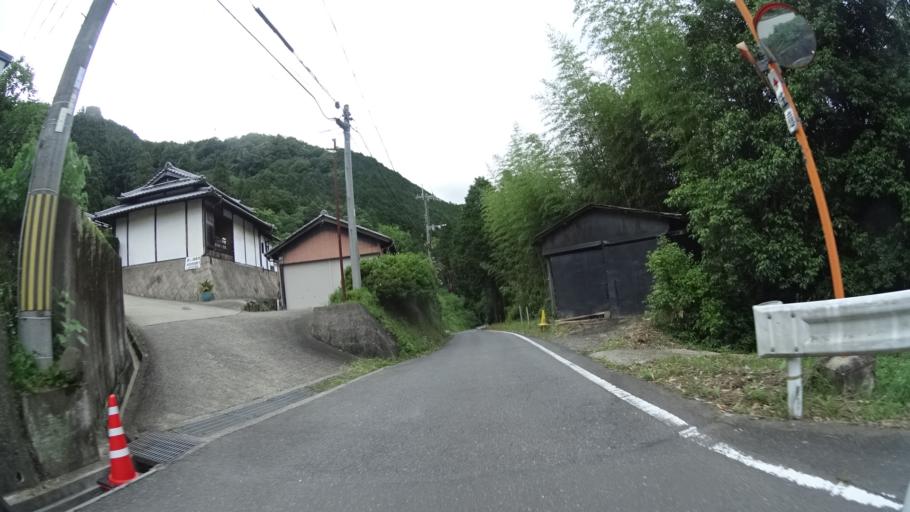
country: JP
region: Nara
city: Nara-shi
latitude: 34.7541
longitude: 135.9268
